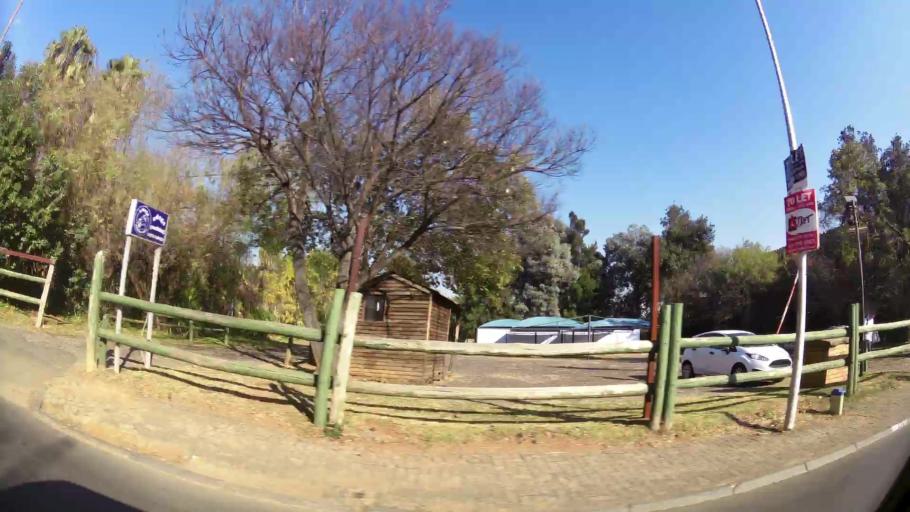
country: ZA
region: Gauteng
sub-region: Ekurhuleni Metropolitan Municipality
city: Germiston
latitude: -26.1774
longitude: 28.1355
